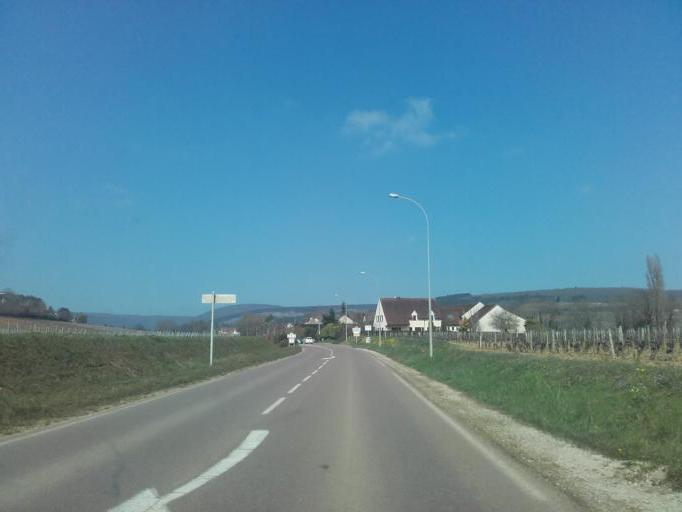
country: FR
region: Bourgogne
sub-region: Departement de la Cote-d'Or
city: Savigny-les-Beaune
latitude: 47.0546
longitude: 4.8370
